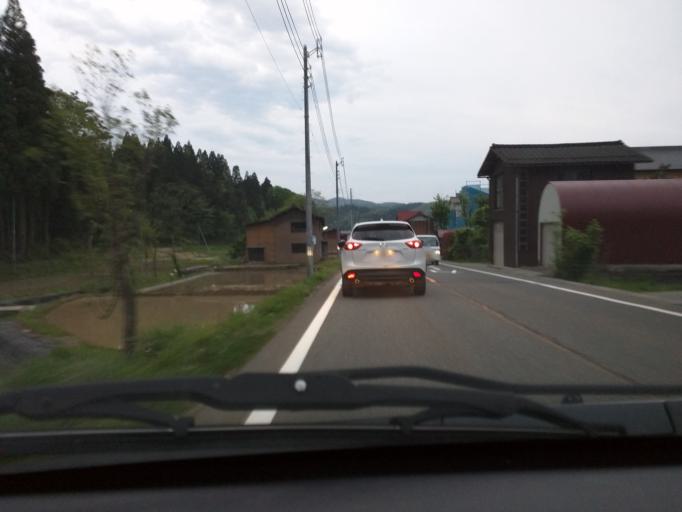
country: JP
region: Niigata
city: Ojiya
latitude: 37.3184
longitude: 138.7226
